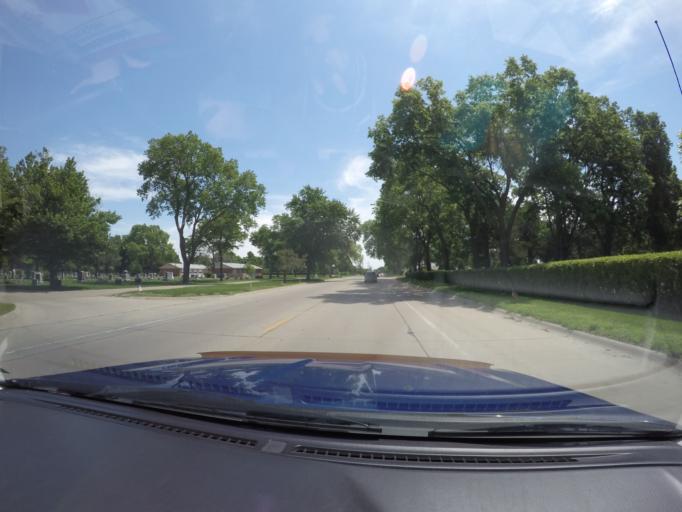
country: US
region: Nebraska
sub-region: Hall County
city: Grand Island
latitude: 40.9026
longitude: -98.3754
